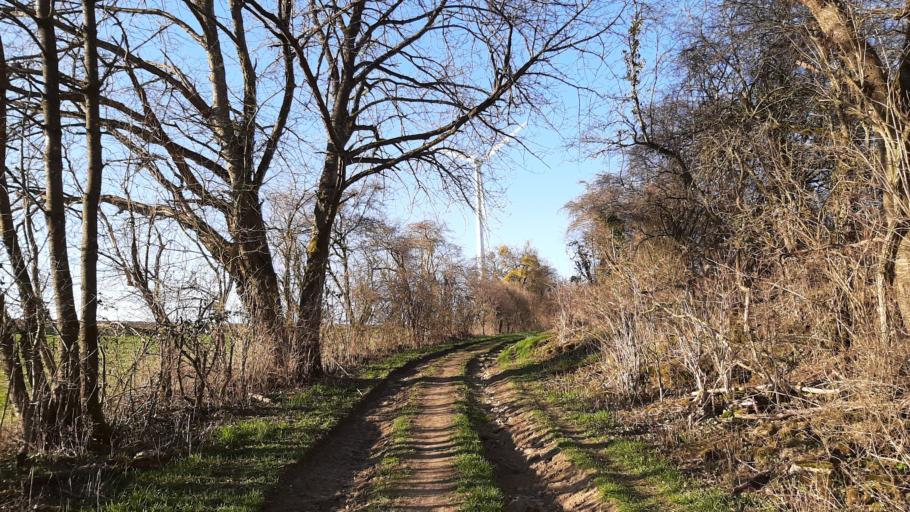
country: LU
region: Grevenmacher
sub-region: Canton d'Echternach
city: Mompach
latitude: 49.7487
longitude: 6.4915
